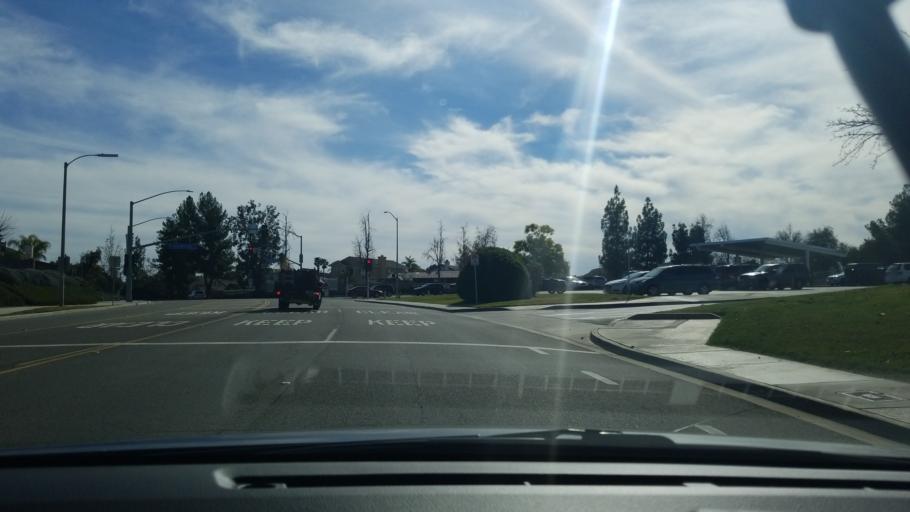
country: US
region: California
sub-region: Riverside County
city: Murrieta Hot Springs
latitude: 33.5663
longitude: -117.1679
